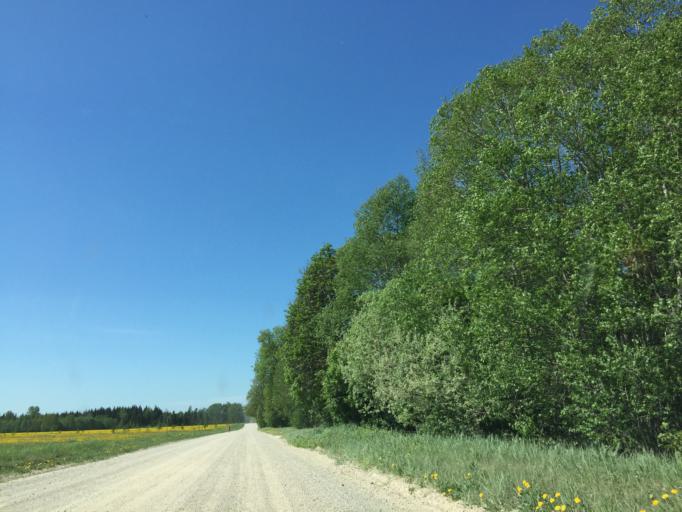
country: LV
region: Kegums
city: Kegums
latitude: 56.8941
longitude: 24.8132
